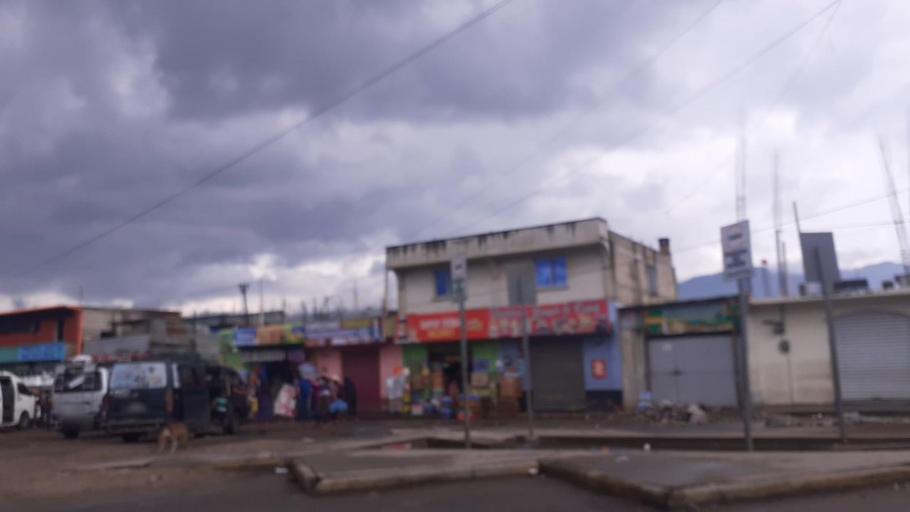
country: GT
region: Quetzaltenango
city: Ostuncalco
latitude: 14.8725
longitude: -91.6233
